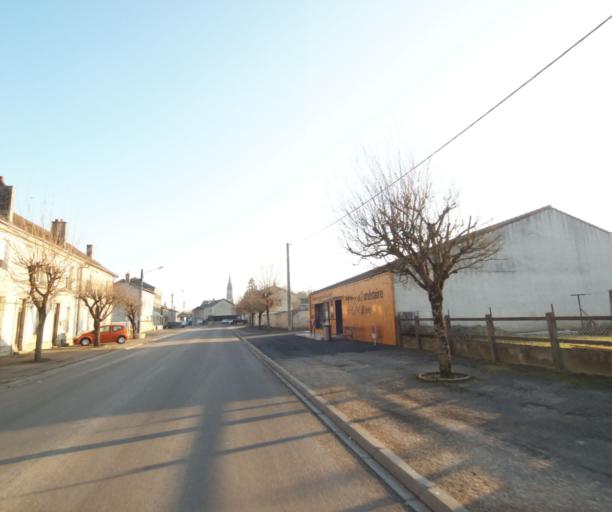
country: FR
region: Champagne-Ardenne
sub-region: Departement de la Haute-Marne
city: Bienville
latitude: 48.5882
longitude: 5.0351
